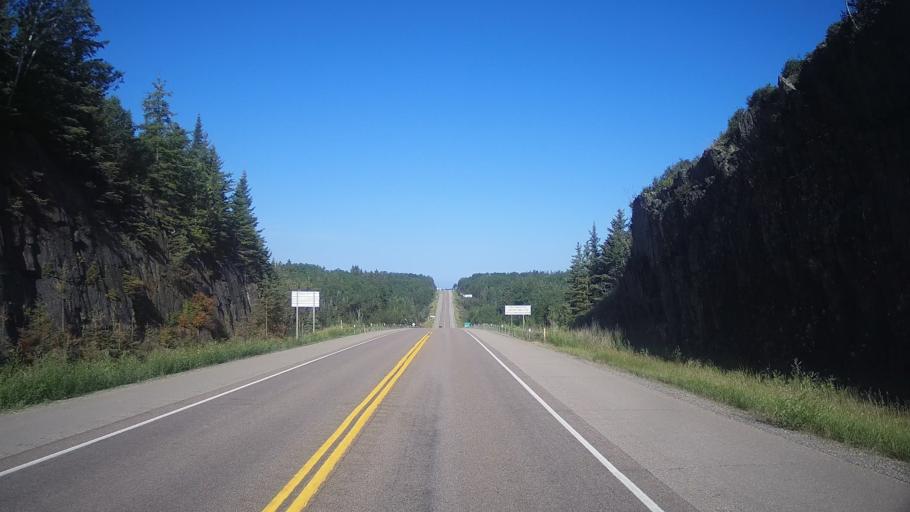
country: US
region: Minnesota
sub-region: Roseau County
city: Warroad
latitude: 49.7374
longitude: -95.1896
